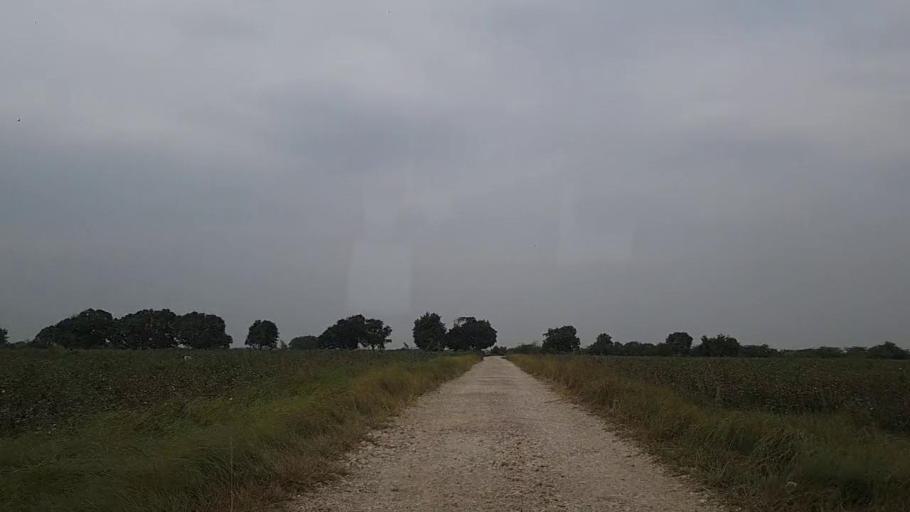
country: PK
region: Sindh
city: Mirpur Sakro
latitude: 24.6195
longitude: 67.7176
